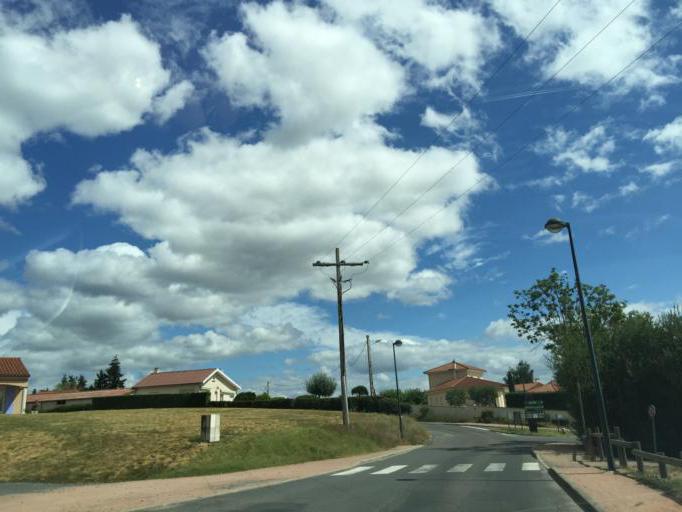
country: FR
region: Rhone-Alpes
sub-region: Departement de la Loire
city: Savigneux
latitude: 45.6135
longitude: 4.0868
